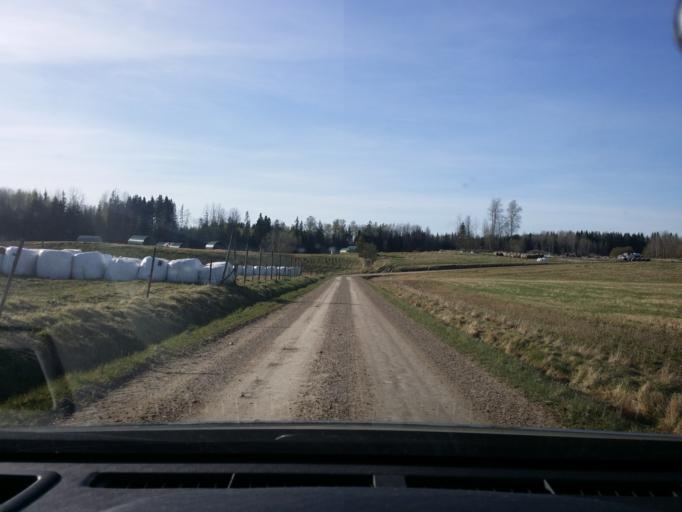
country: SE
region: Dalarna
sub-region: Avesta Kommun
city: Avesta
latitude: 60.0736
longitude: 16.3673
